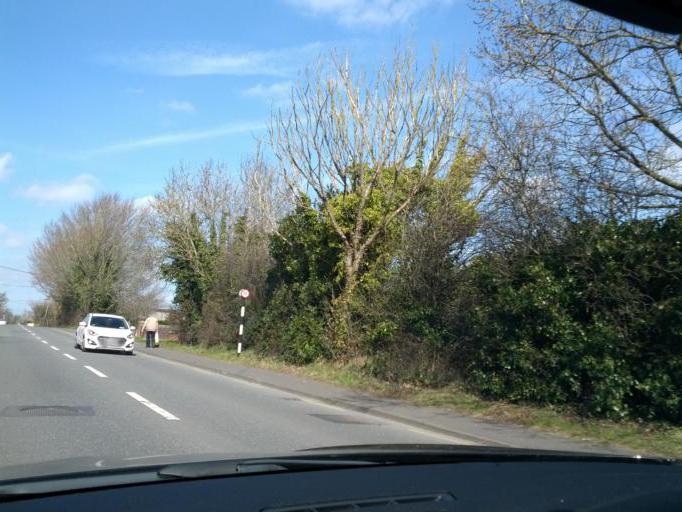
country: IE
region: Leinster
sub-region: Kildare
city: Maynooth
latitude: 53.3867
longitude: -6.5963
